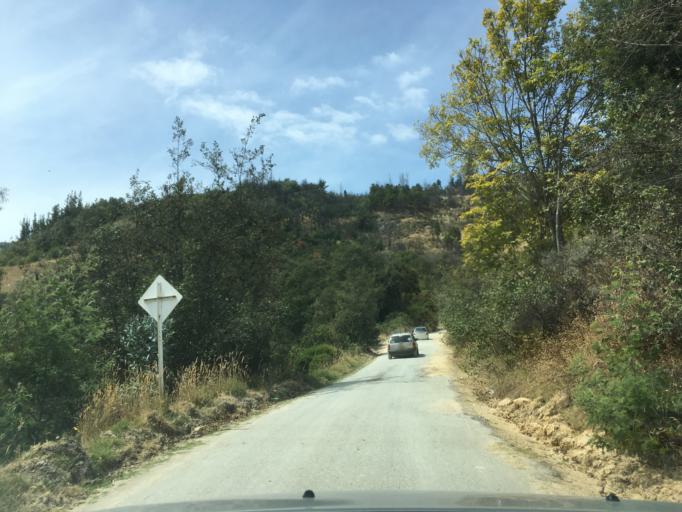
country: CO
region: Boyaca
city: Aquitania
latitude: 5.5872
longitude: -72.9215
